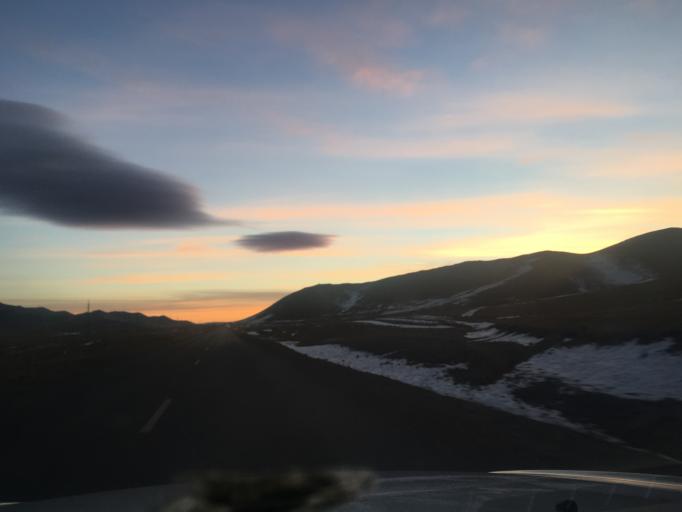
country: MN
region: Central Aimak
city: Mandal
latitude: 48.1169
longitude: 106.6446
